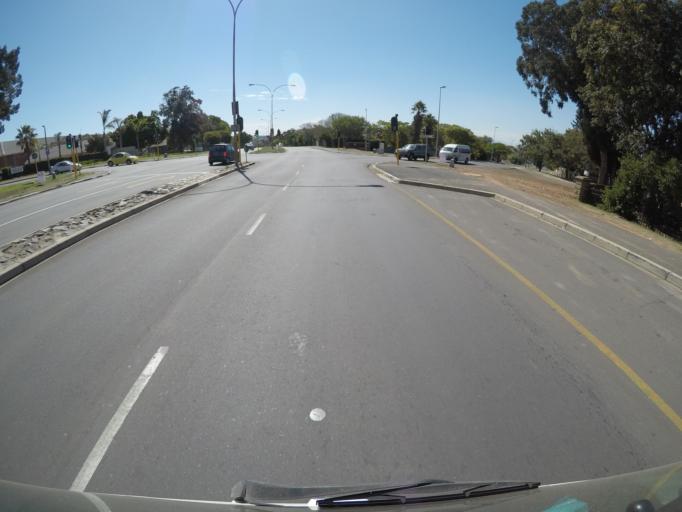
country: ZA
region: Western Cape
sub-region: City of Cape Town
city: Kraaifontein
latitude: -33.8376
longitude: 18.6492
